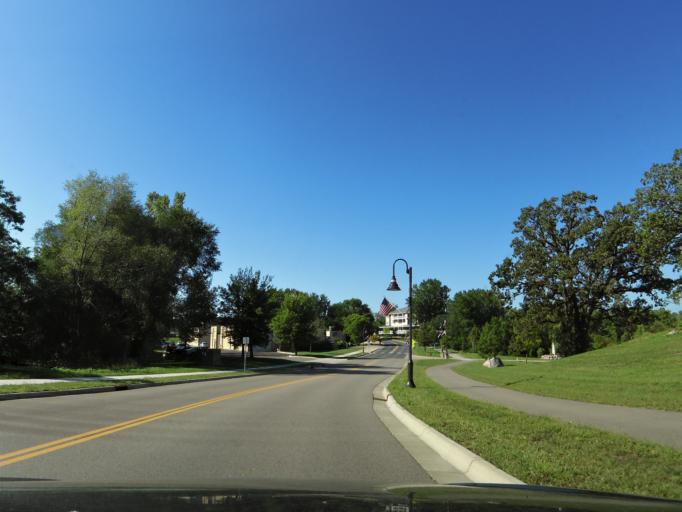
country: US
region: Minnesota
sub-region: Scott County
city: Prior Lake
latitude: 44.7169
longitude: -93.4216
